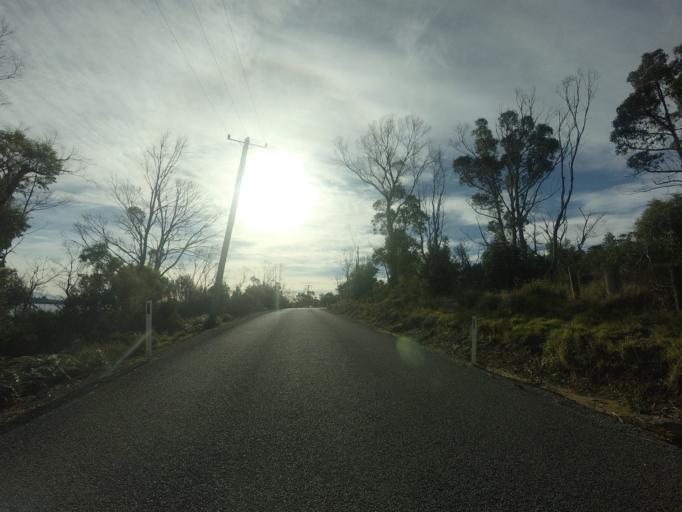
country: AU
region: Tasmania
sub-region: Sorell
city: Sorell
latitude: -42.9548
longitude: 147.8516
